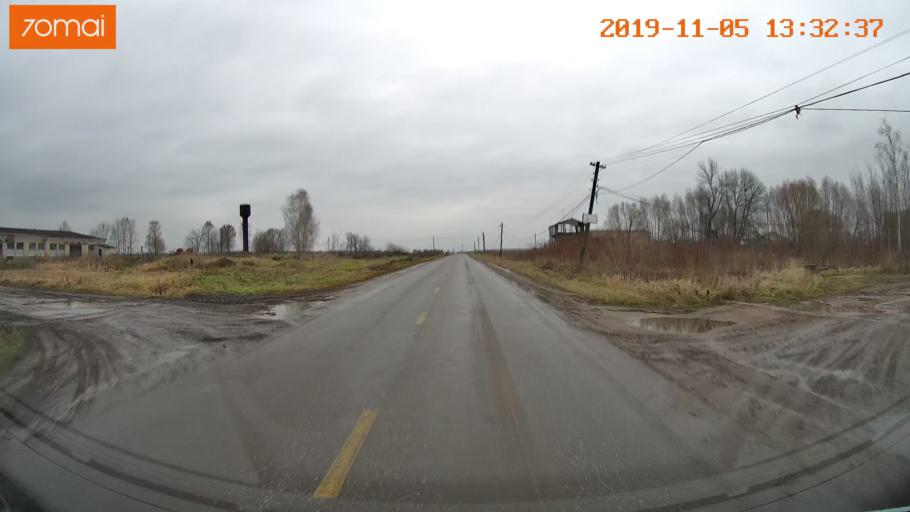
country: RU
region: Ivanovo
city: Shuya
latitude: 56.8846
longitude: 41.3973
